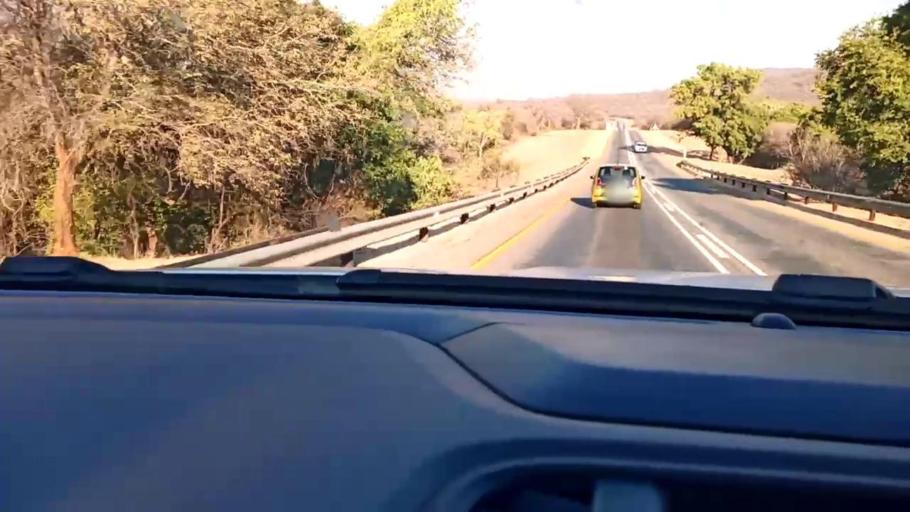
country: ZA
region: Limpopo
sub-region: Mopani District Municipality
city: Duiwelskloof
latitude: -23.6296
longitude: 30.1326
